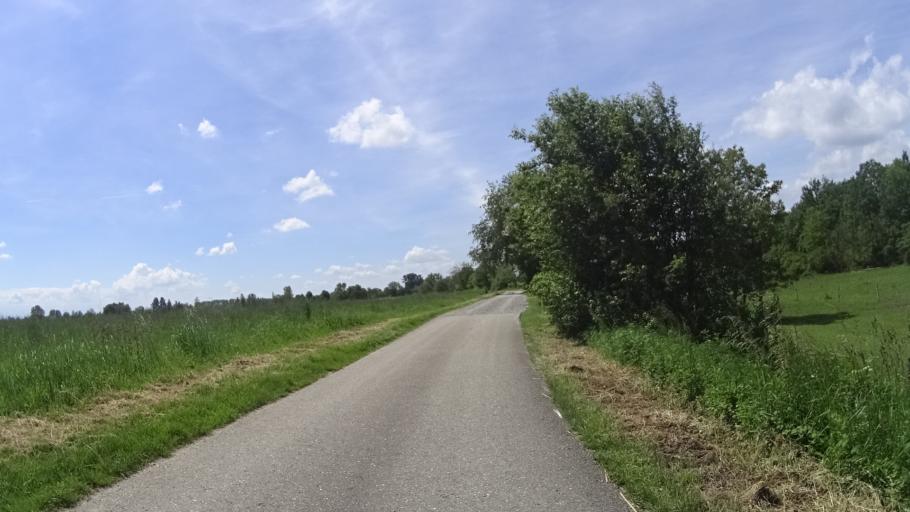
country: DE
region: Baden-Wuerttemberg
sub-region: Freiburg Region
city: Kappel-Grafenhausen
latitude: 48.3077
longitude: 7.7399
